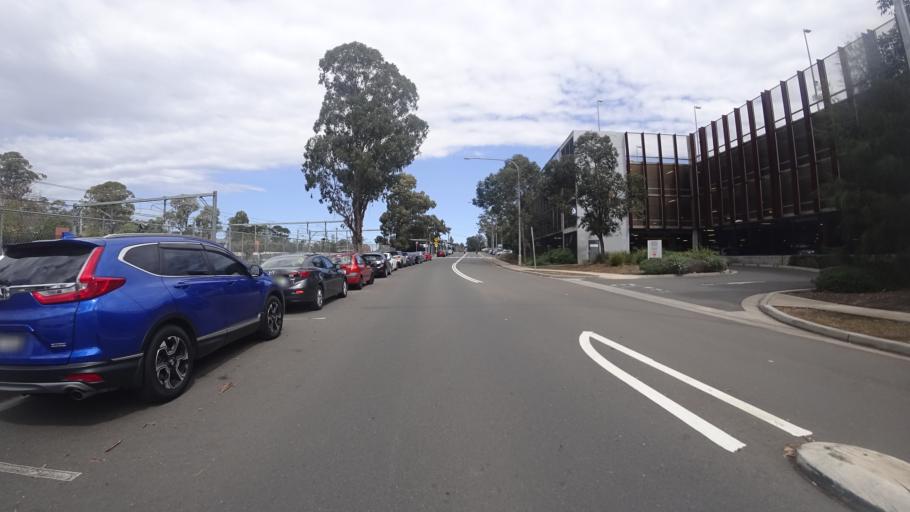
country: AU
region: New South Wales
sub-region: Campbelltown Municipality
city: Glenfield
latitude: -33.9692
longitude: 150.8960
